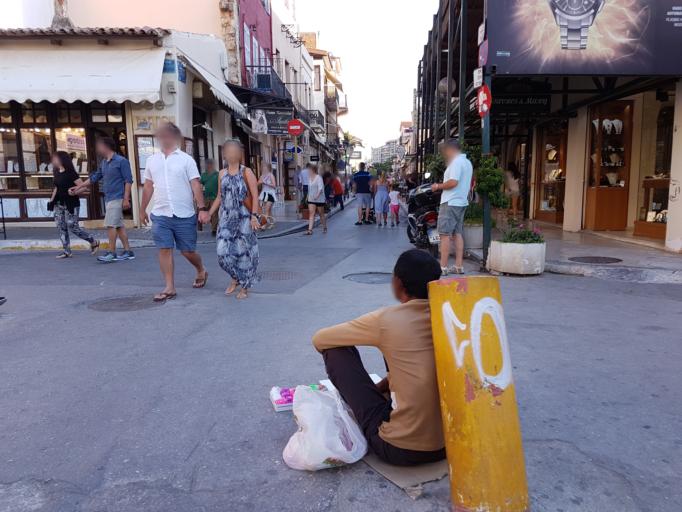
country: GR
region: Crete
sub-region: Nomos Chanias
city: Chania
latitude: 35.5163
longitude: 24.0179
